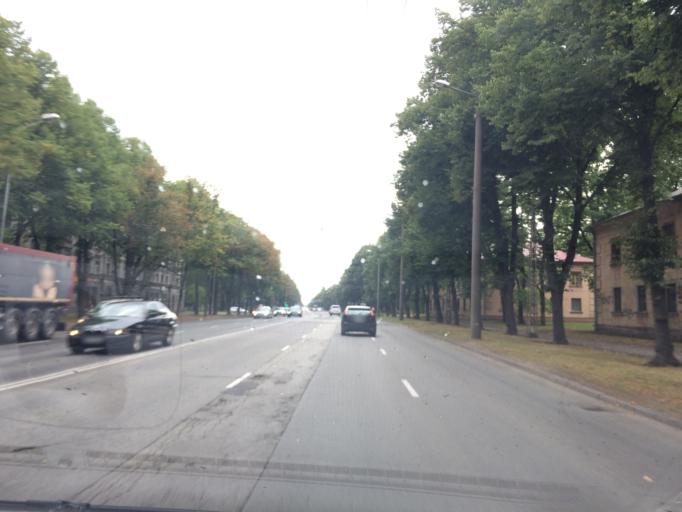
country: LV
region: Riga
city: Jaunciems
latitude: 56.9832
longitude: 24.1994
